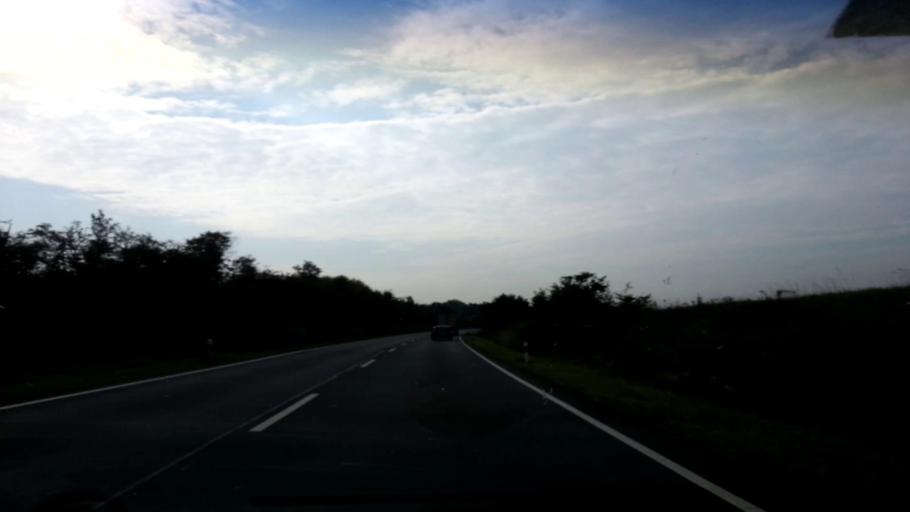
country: DE
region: Bavaria
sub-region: Regierungsbezirk Unterfranken
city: Prichsenstadt
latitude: 49.8394
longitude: 10.3529
